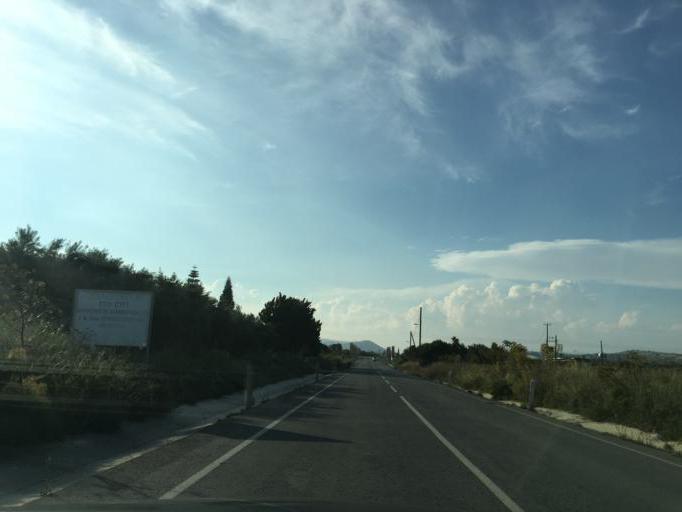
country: CY
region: Larnaka
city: Kofinou
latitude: 34.7453
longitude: 33.3216
